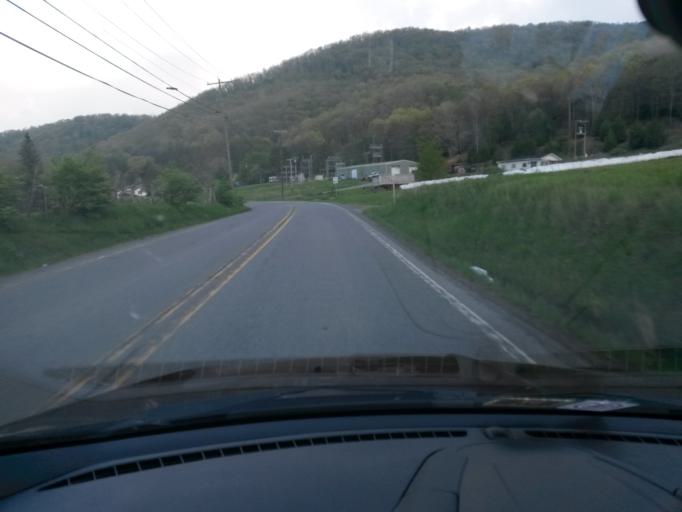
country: US
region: Virginia
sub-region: Highland County
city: Monterey
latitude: 38.5479
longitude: -79.8014
